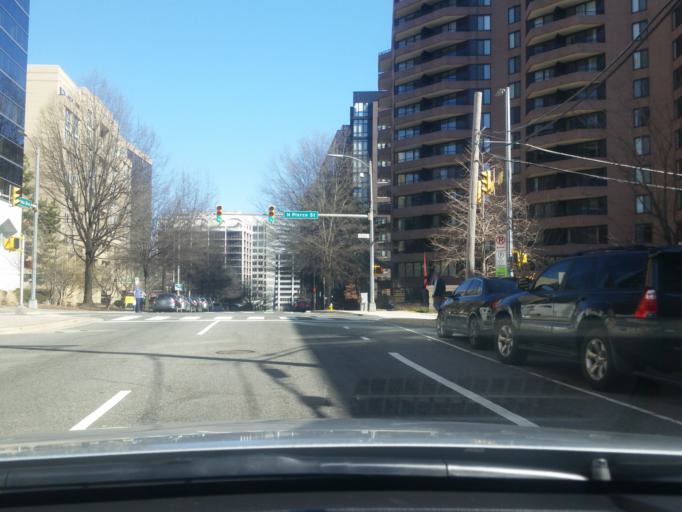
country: US
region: Virginia
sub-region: Arlington County
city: Arlington
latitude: 38.8933
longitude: -77.0770
